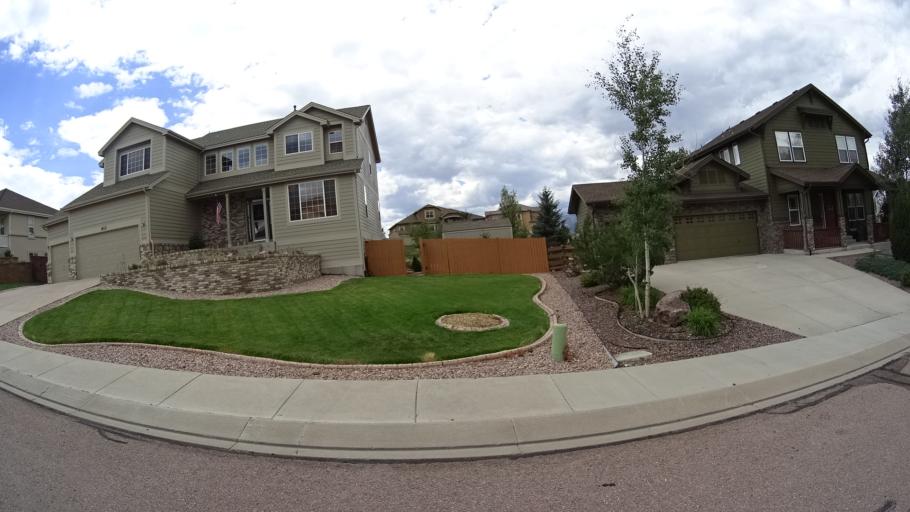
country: US
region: Colorado
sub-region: El Paso County
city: Gleneagle
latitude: 39.0318
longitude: -104.8126
